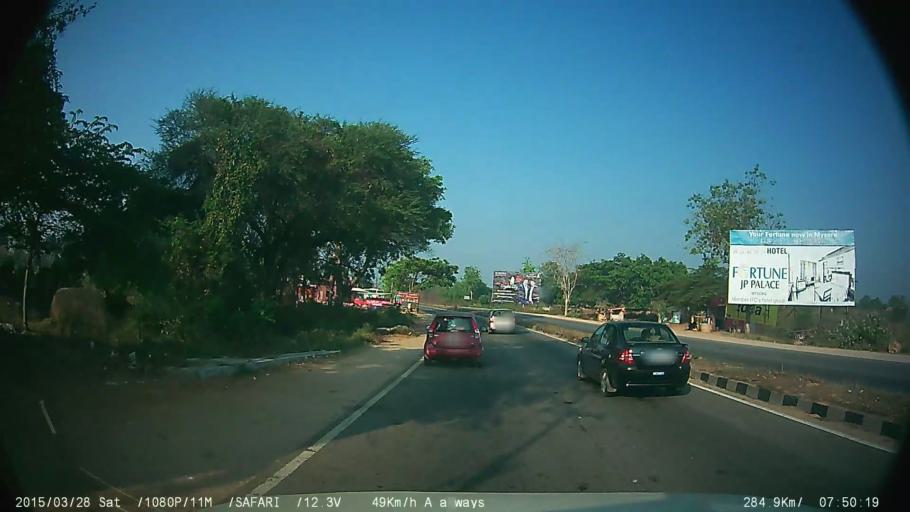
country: IN
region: Karnataka
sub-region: Mandya
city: Shrirangapattana
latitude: 12.4676
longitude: 76.7533
